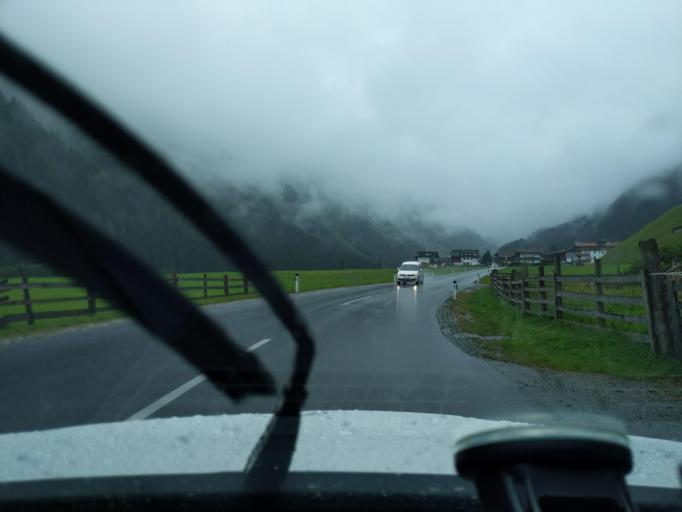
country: AT
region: Tyrol
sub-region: Politischer Bezirk Innsbruck Land
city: Schmirn
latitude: 47.1317
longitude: 11.7009
